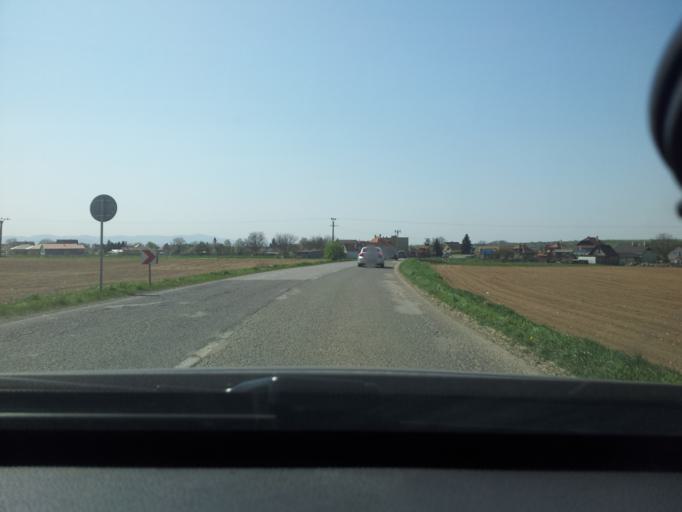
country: SK
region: Nitriansky
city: Banovce nad Bebravou
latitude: 48.6988
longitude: 18.2496
